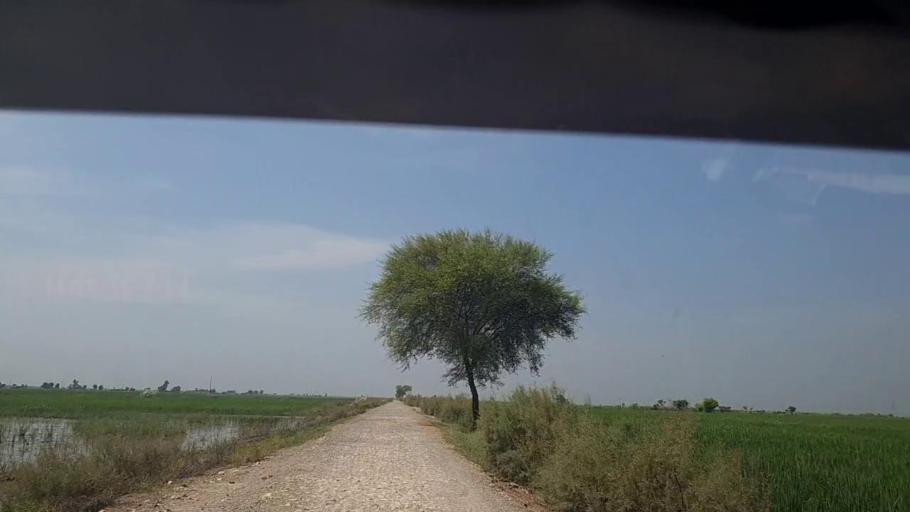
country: PK
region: Sindh
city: Thul
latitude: 28.2126
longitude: 68.6848
